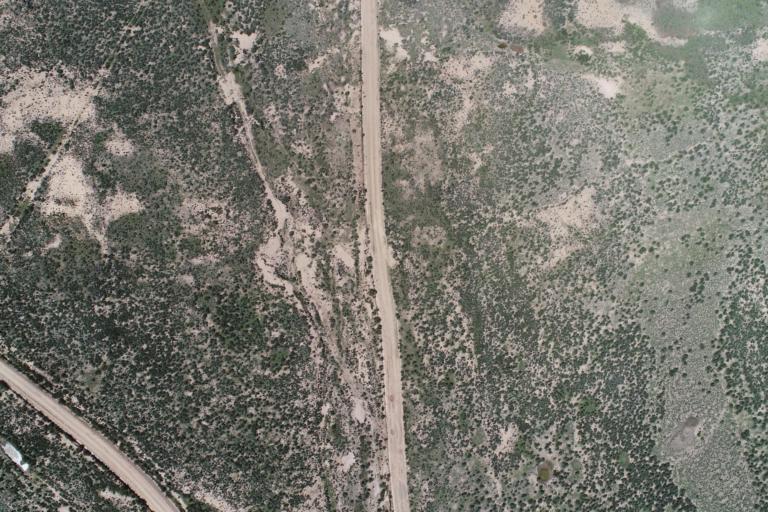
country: BO
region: La Paz
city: Patacamaya
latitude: -17.2923
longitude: -68.4855
